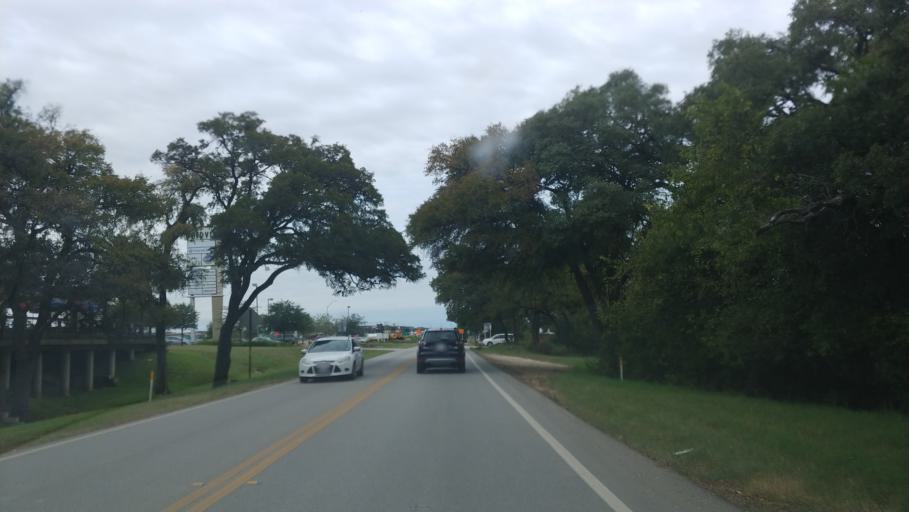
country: US
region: Texas
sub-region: Bexar County
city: Cross Mountain
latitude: 29.6687
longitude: -98.6311
